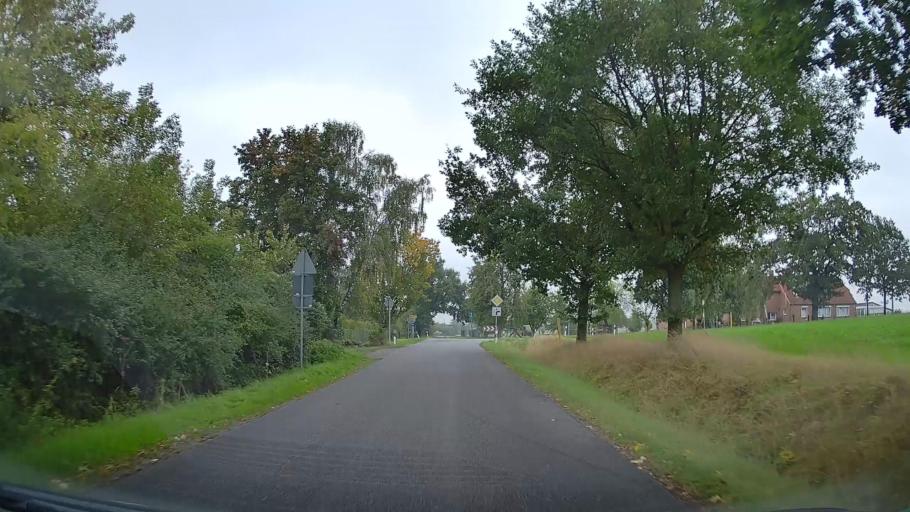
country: DE
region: Mecklenburg-Vorpommern
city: Hornstorf
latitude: 53.9038
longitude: 11.5123
